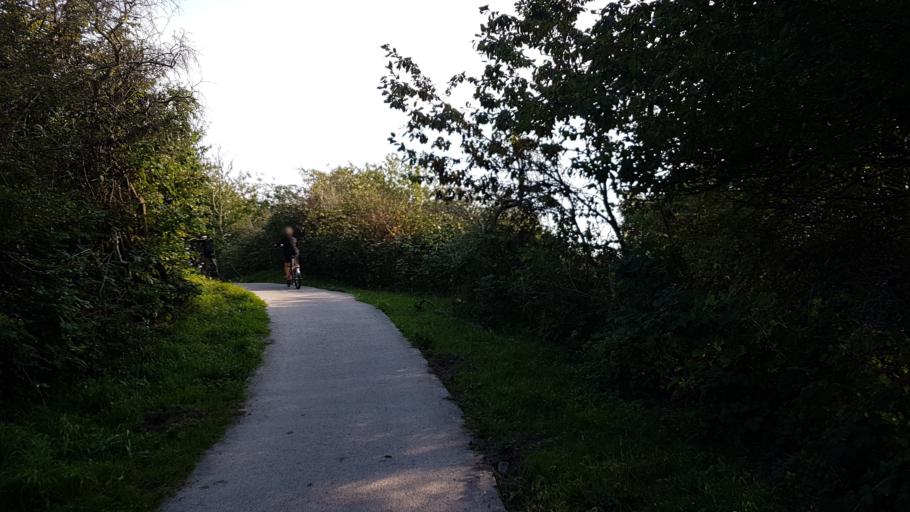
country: DE
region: Mecklenburg-Vorpommern
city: Glowe
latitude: 54.5597
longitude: 13.4903
